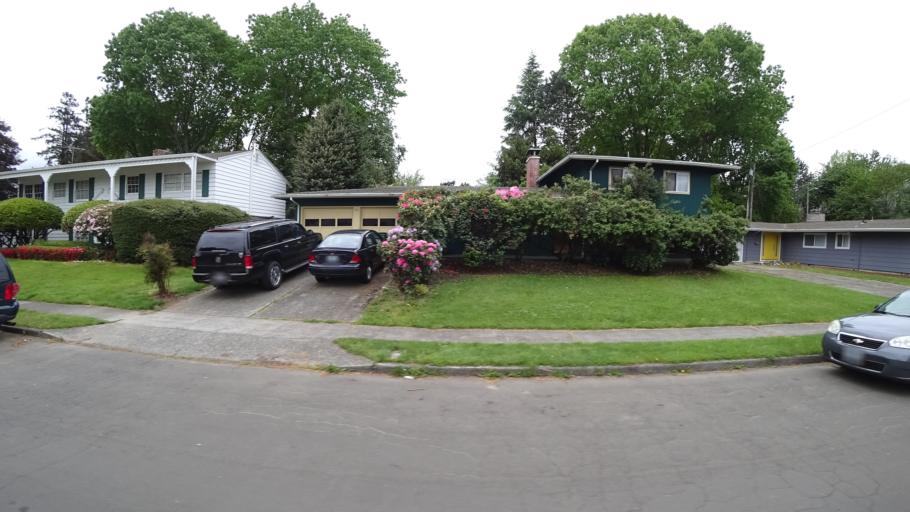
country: US
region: Oregon
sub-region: Washington County
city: Beaverton
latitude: 45.4727
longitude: -122.8024
